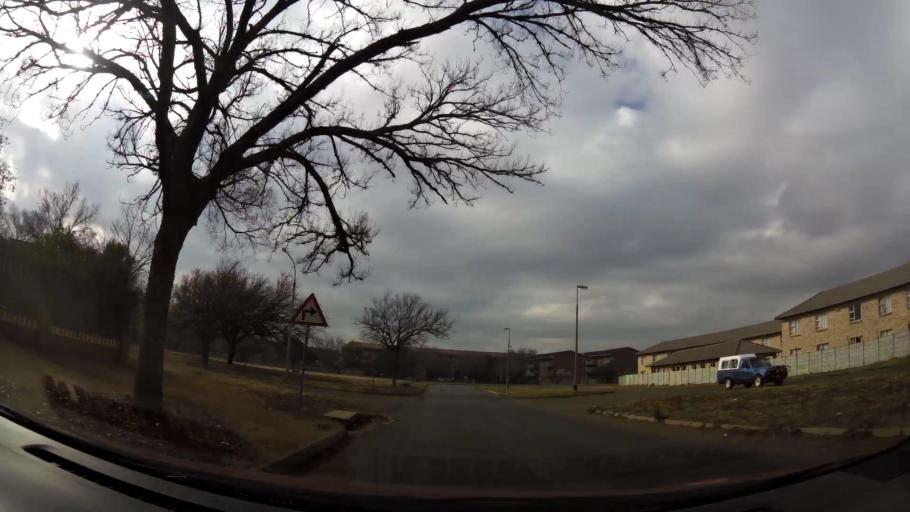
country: ZA
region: Gauteng
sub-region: Sedibeng District Municipality
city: Vanderbijlpark
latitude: -26.6930
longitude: 27.8392
